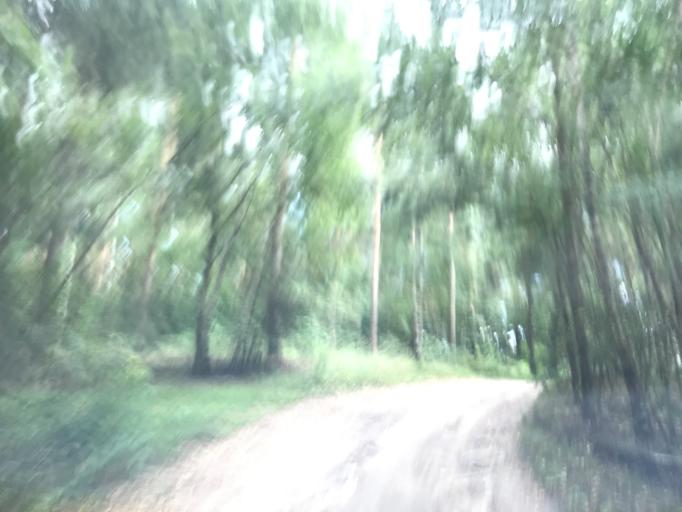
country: PL
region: Kujawsko-Pomorskie
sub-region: Powiat brodnicki
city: Brzozie
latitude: 53.3242
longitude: 19.6880
